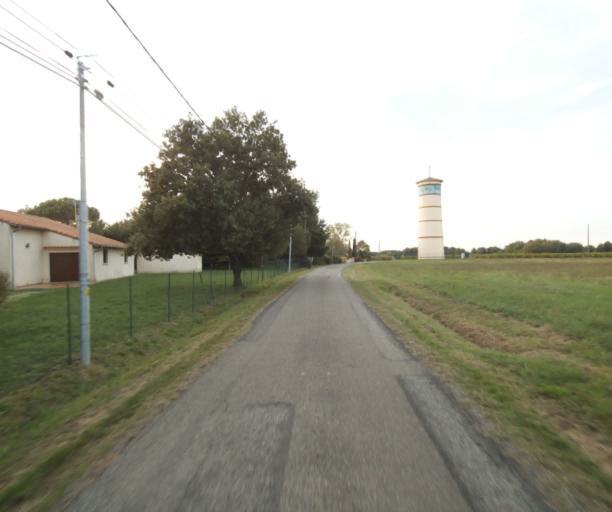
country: FR
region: Midi-Pyrenees
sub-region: Departement du Tarn-et-Garonne
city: Pompignan
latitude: 43.8213
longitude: 1.3184
